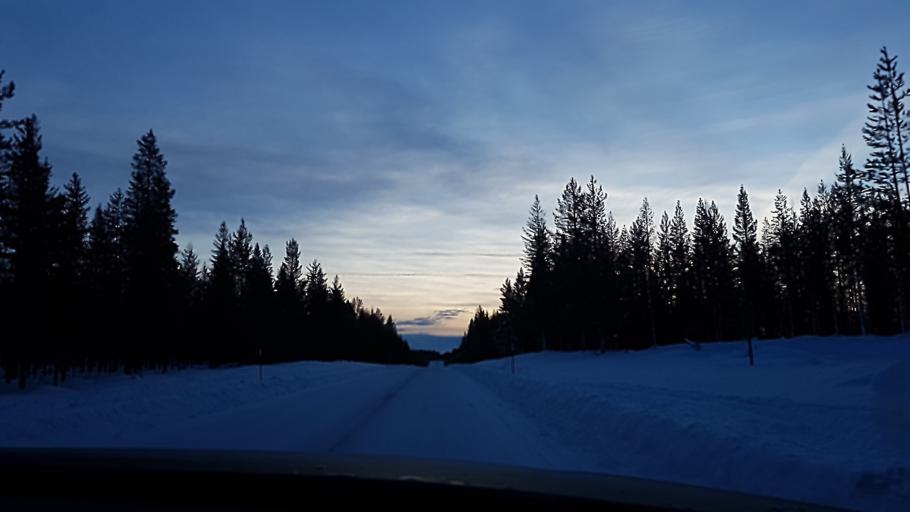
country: SE
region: Norrbotten
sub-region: Arvidsjaurs Kommun
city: Arvidsjaur
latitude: 65.9153
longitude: 19.4614
